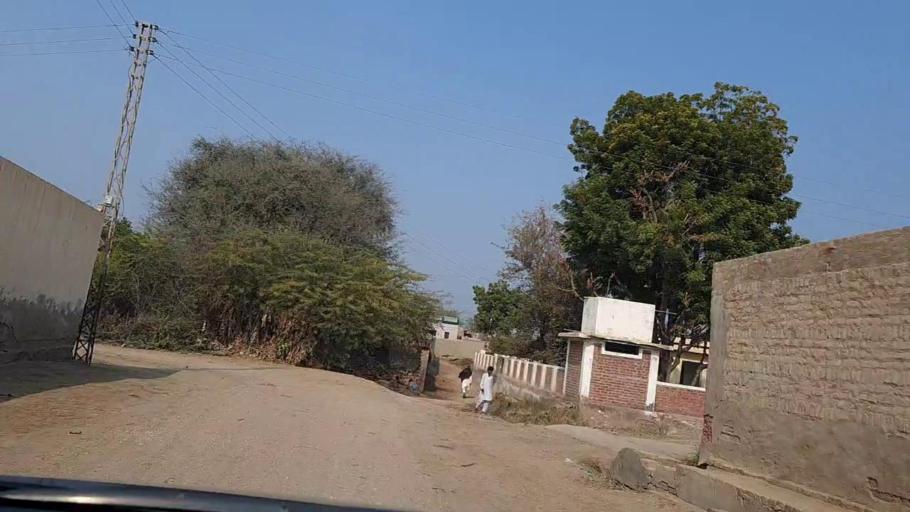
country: PK
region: Sindh
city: Sakrand
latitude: 26.1524
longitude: 68.2496
